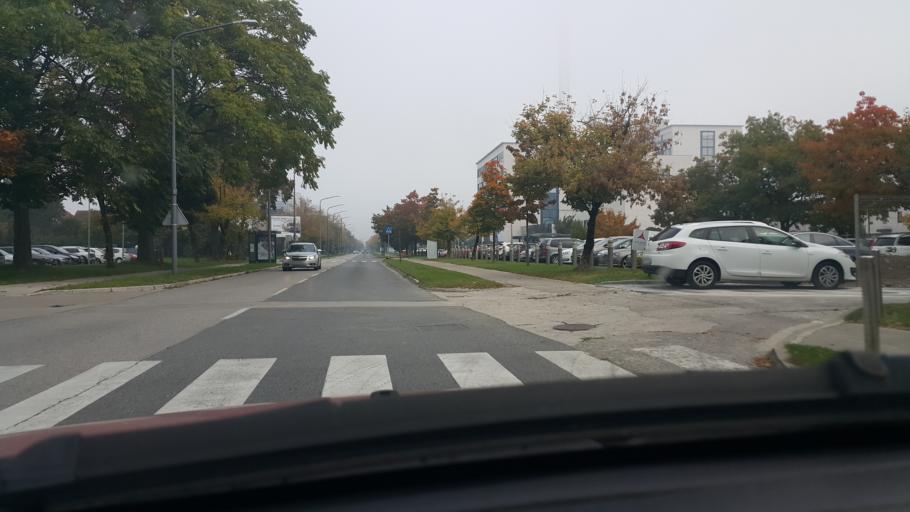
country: SI
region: Ljubljana
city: Ljubljana
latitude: 46.0731
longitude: 14.4992
